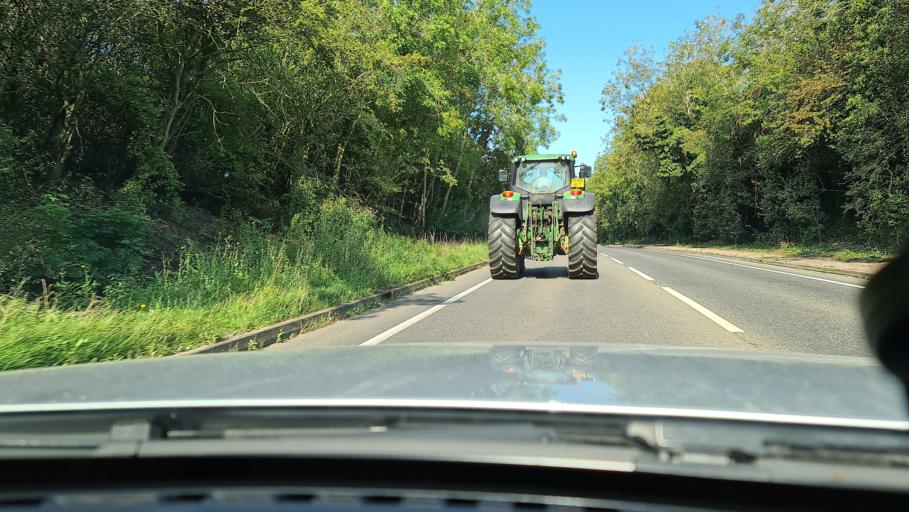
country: GB
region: England
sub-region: Northamptonshire
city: Bugbrooke
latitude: 52.2056
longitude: -1.0461
